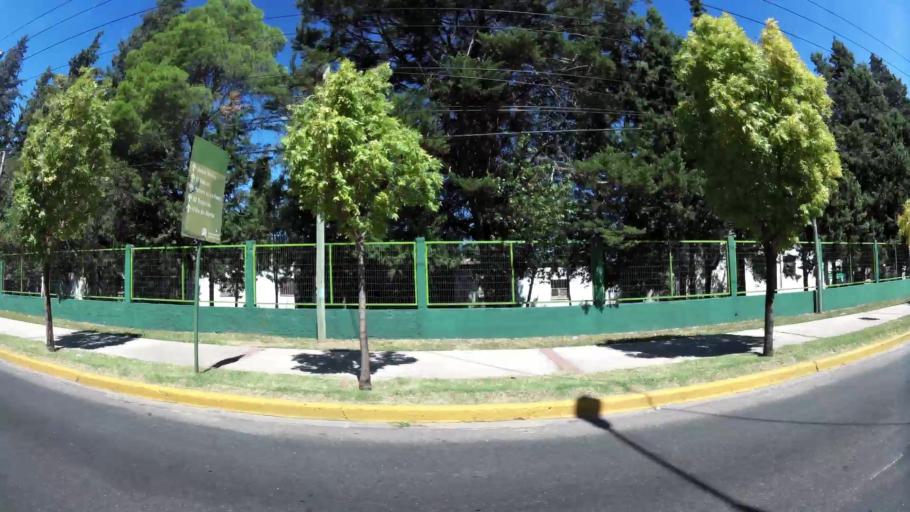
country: AR
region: San Luis
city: San Luis
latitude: -33.2943
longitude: -66.3049
